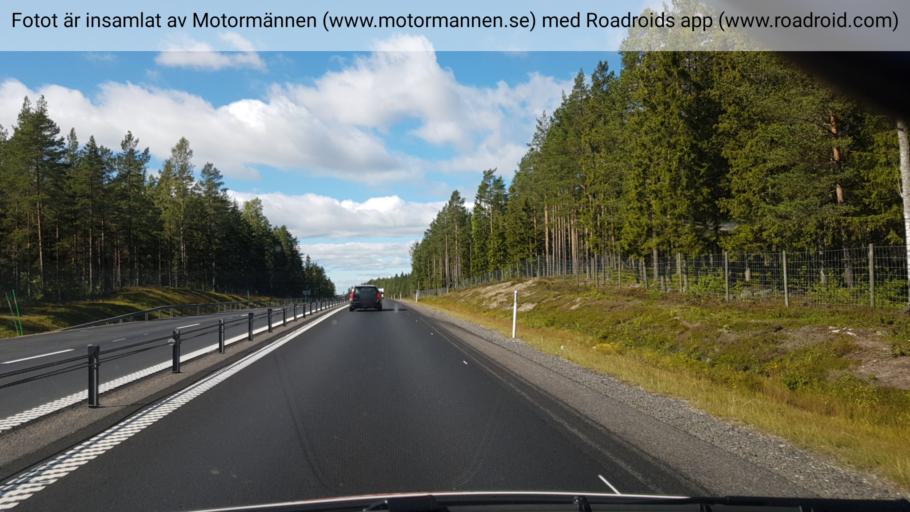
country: SE
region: Vaesterbotten
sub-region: Umea Kommun
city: Hoernefors
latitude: 63.5986
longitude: 19.7395
